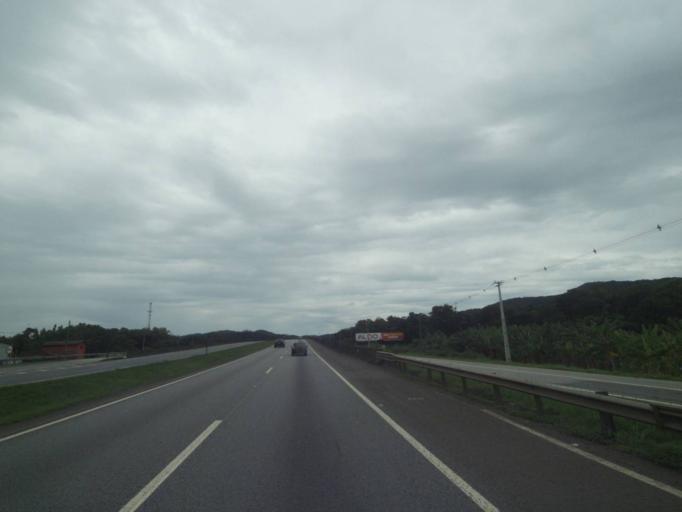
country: BR
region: Parana
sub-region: Antonina
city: Antonina
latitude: -25.5493
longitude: -48.7938
